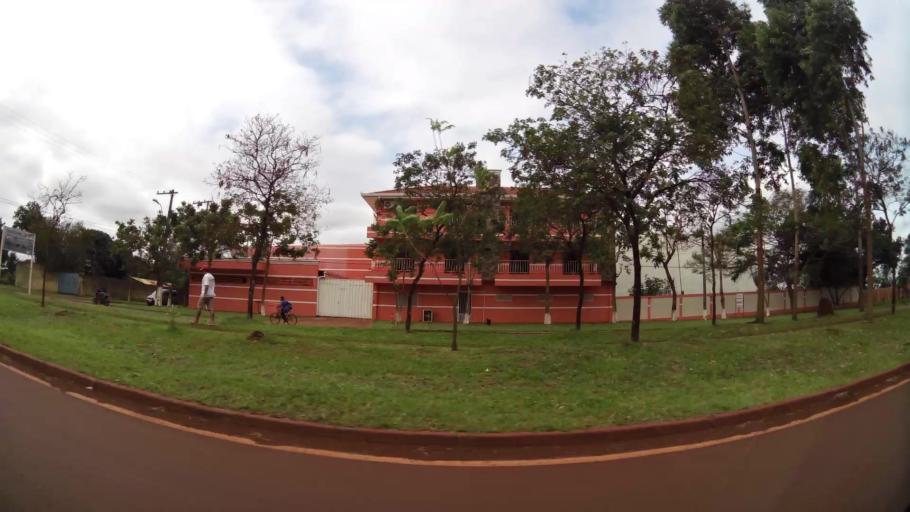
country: PY
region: Alto Parana
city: Ciudad del Este
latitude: -25.3831
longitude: -54.6475
